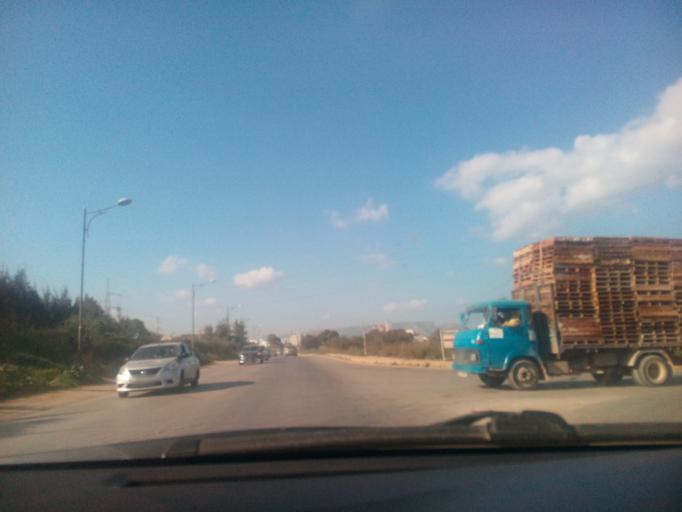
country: DZ
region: Oran
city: Es Senia
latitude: 35.6752
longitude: -0.5916
